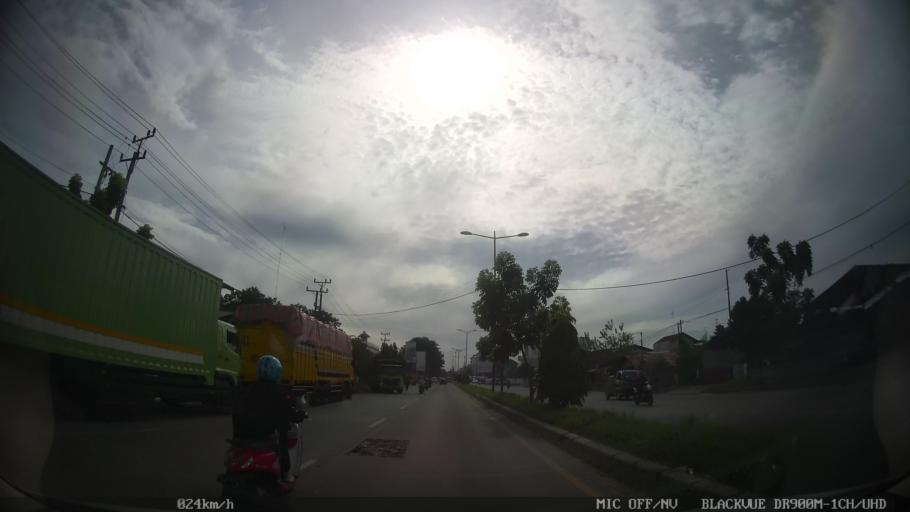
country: ID
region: North Sumatra
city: Medan
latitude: 3.6293
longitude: 98.6913
